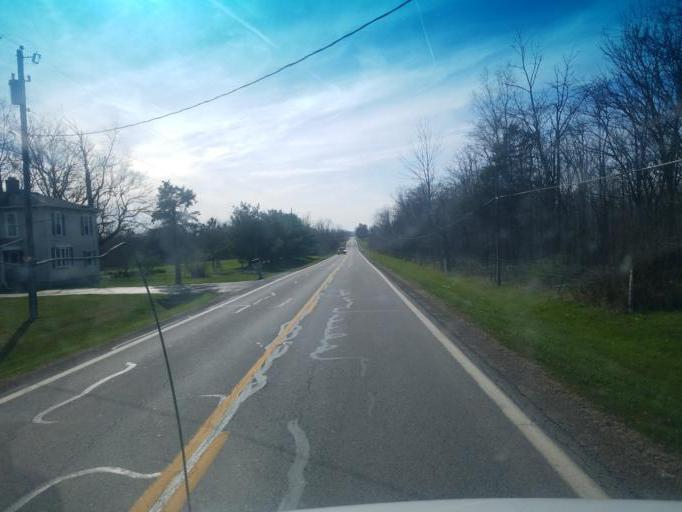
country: US
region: Ohio
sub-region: Champaign County
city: North Lewisburg
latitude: 40.3396
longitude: -83.4783
